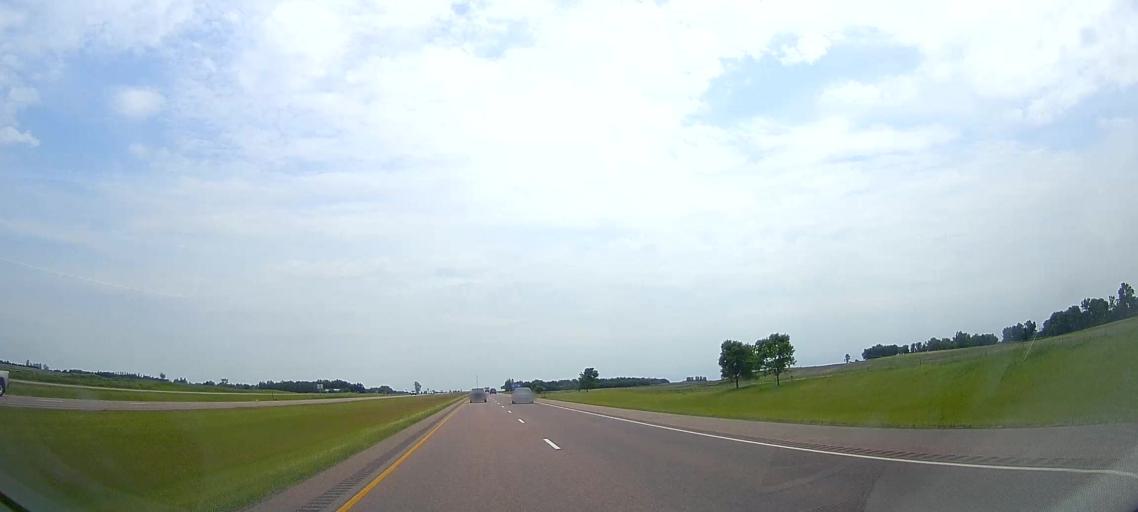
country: US
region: South Dakota
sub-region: Minnehaha County
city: Hartford
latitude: 43.6524
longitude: -97.1011
